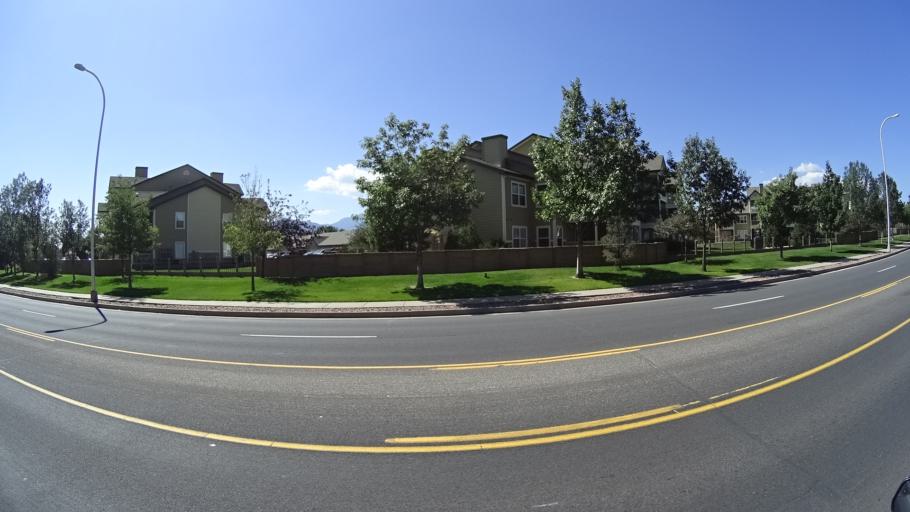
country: US
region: Colorado
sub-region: El Paso County
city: Stratmoor
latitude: 38.8166
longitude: -104.7457
